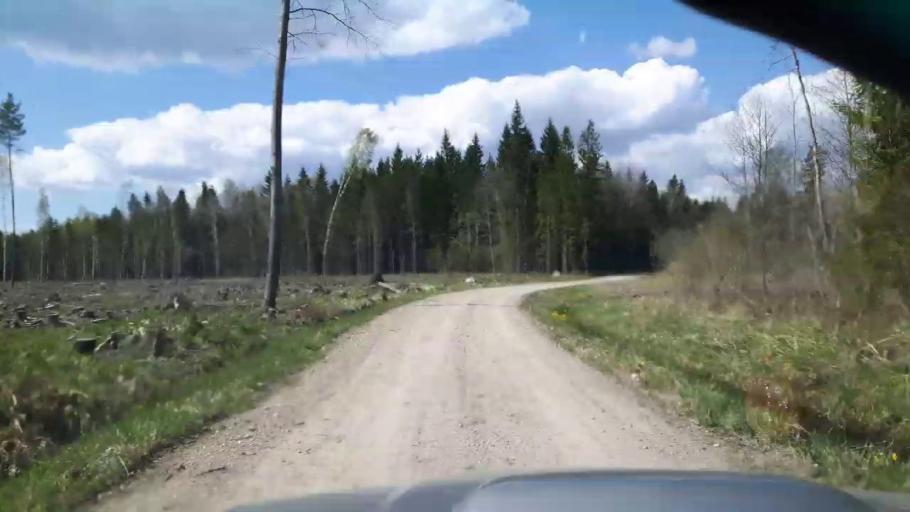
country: EE
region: Paernumaa
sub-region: Tootsi vald
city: Tootsi
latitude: 58.4539
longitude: 24.8887
